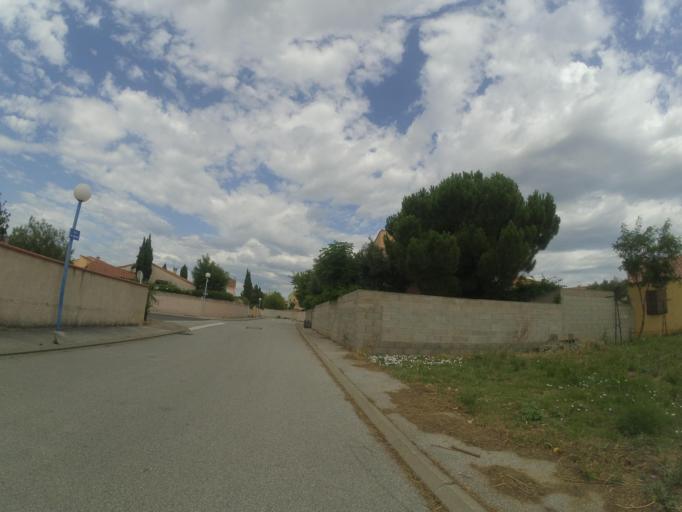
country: FR
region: Languedoc-Roussillon
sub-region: Departement des Pyrenees-Orientales
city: Villeneuve-la-Riviere
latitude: 42.6829
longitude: 2.8050
